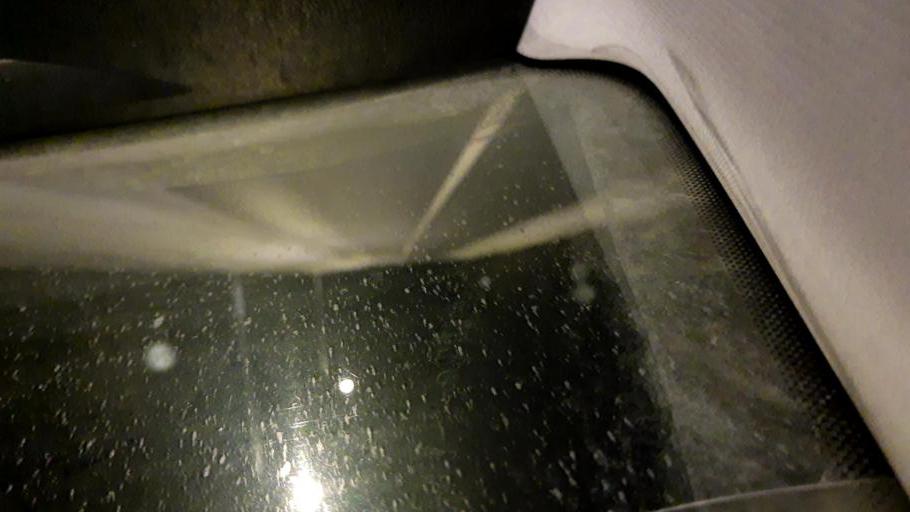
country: RU
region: Moskovskaya
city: Konstantinovo
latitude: 56.6985
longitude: 38.1266
